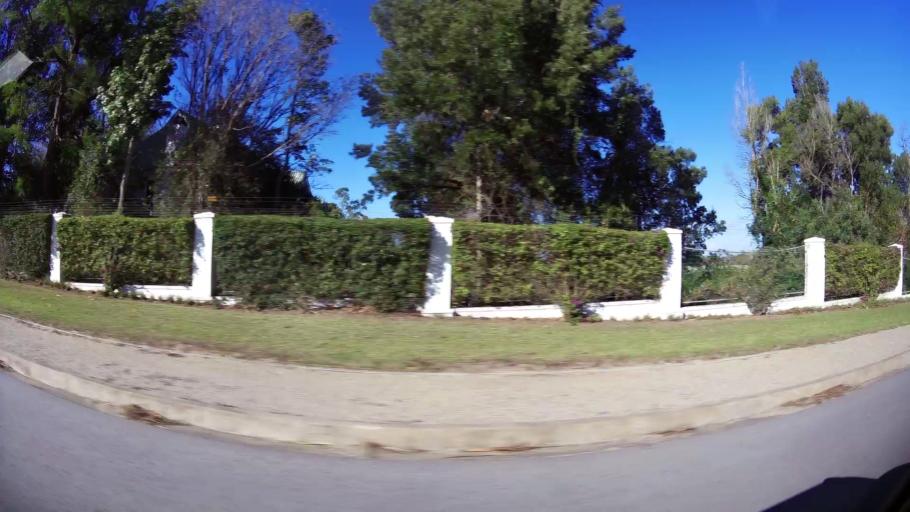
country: ZA
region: Western Cape
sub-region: Eden District Municipality
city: George
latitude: -33.9523
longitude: 22.4039
